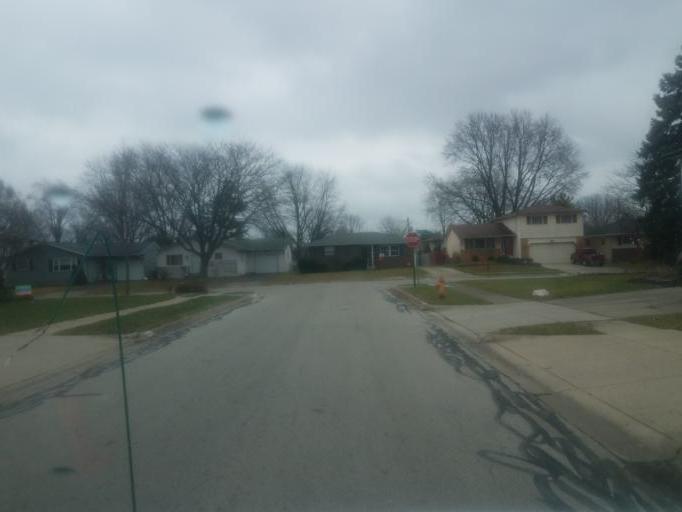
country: US
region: Ohio
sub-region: Franklin County
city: Minerva Park
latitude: 40.0820
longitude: -82.9591
